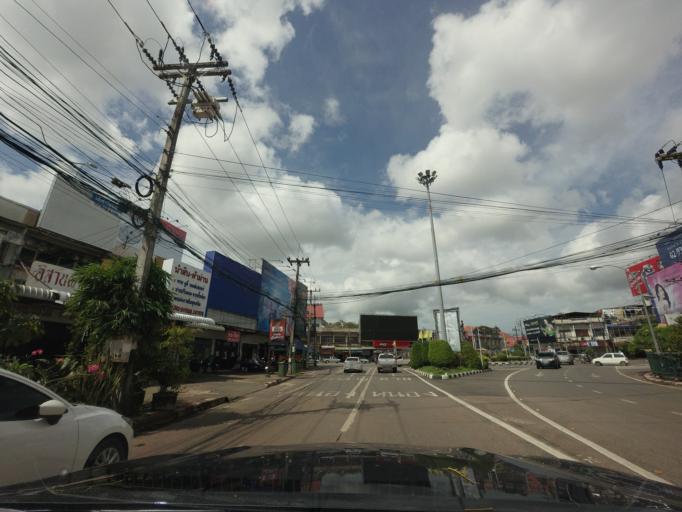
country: TH
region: Changwat Udon Thani
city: Udon Thani
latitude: 17.4008
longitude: 102.7953
